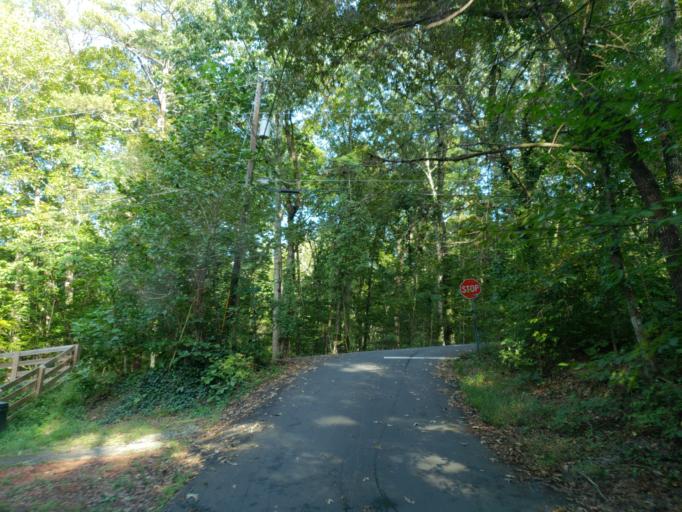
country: US
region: Georgia
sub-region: Fulton County
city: Roswell
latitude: 34.0823
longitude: -84.4104
